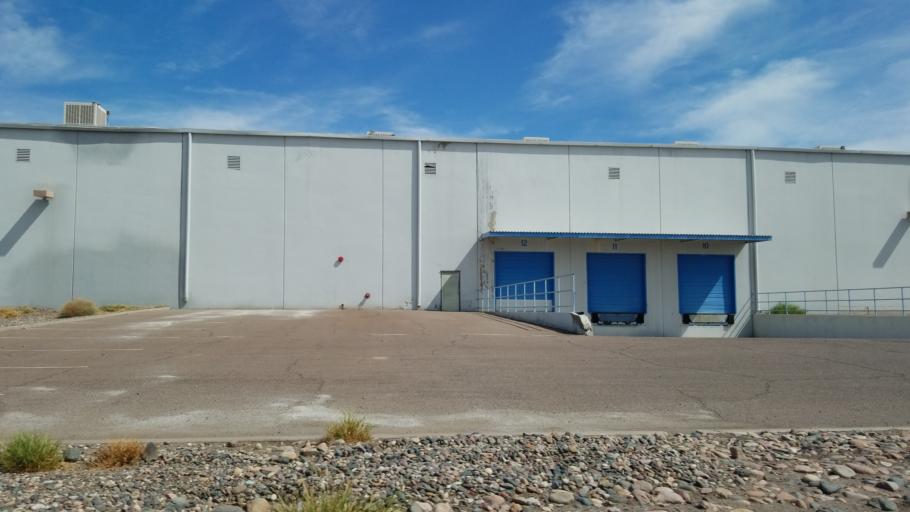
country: US
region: Arizona
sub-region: Maricopa County
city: Tolleson
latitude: 33.4479
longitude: -112.1884
